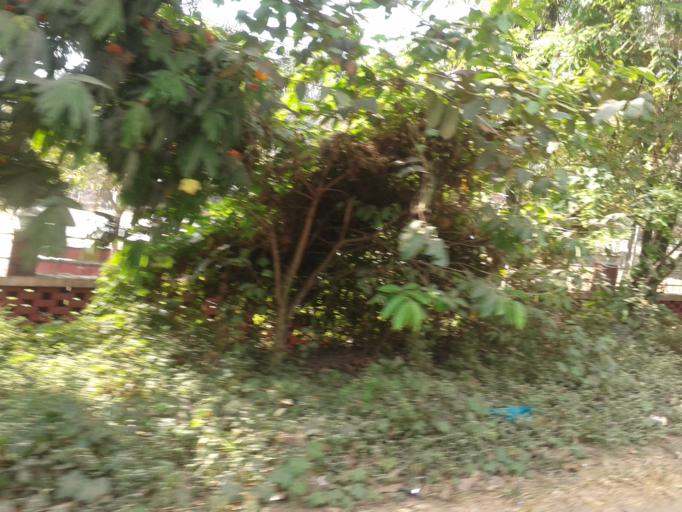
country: IN
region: Kerala
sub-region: Thrissur District
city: Kizhake Chalakudi
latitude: 10.3042
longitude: 76.3280
